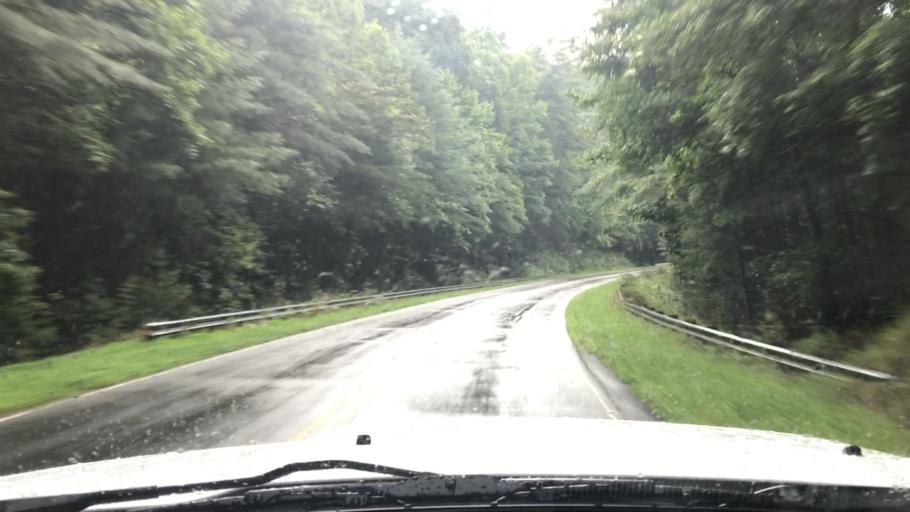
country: US
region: North Carolina
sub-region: Graham County
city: Robbinsville
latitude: 35.3809
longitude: -83.8615
